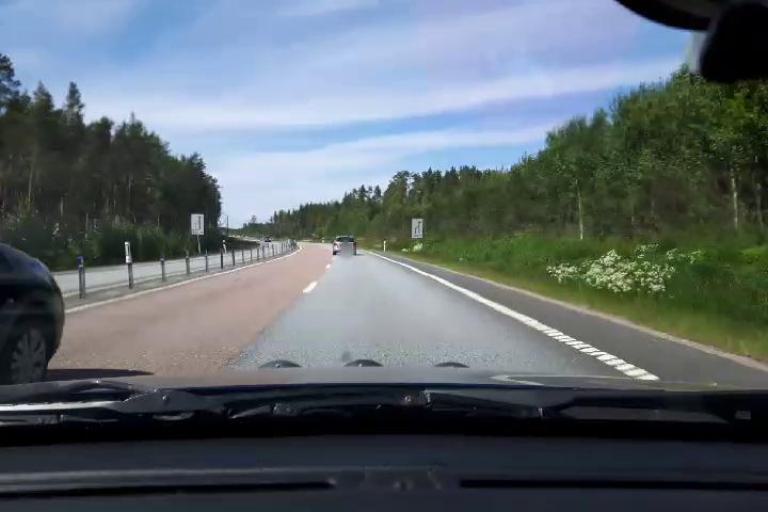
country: SE
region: Gaevleborg
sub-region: Gavle Kommun
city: Norrsundet
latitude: 61.0300
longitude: 16.9750
